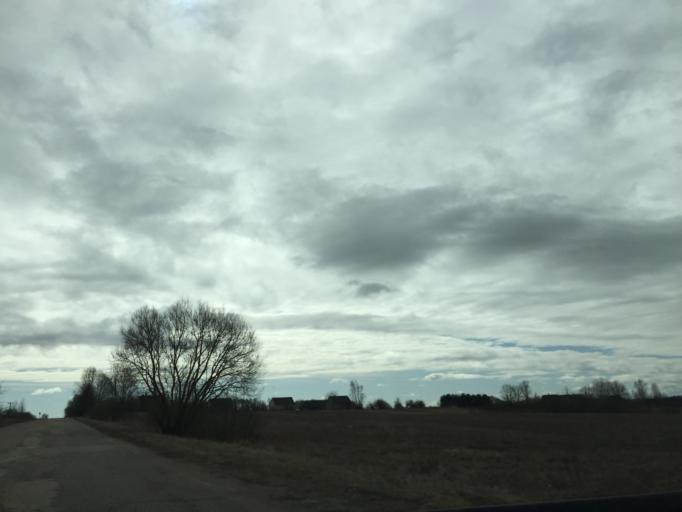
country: LV
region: Daugavpils
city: Daugavpils
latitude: 55.9218
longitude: 26.7398
